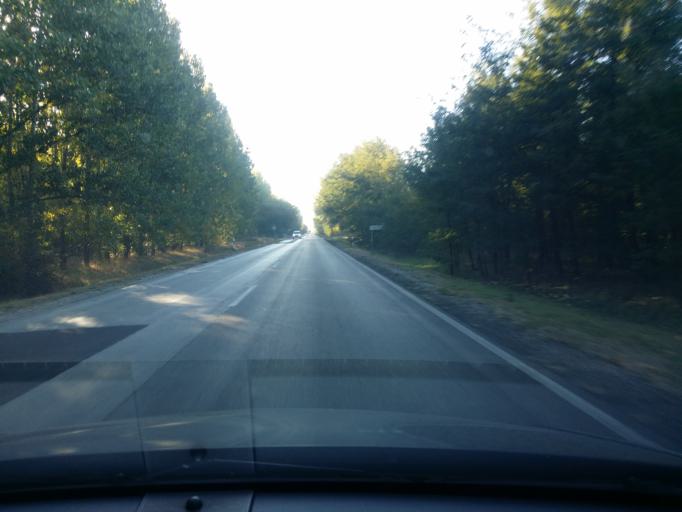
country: HU
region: Bacs-Kiskun
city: Nyarlorinc
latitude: 46.8868
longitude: 19.8372
